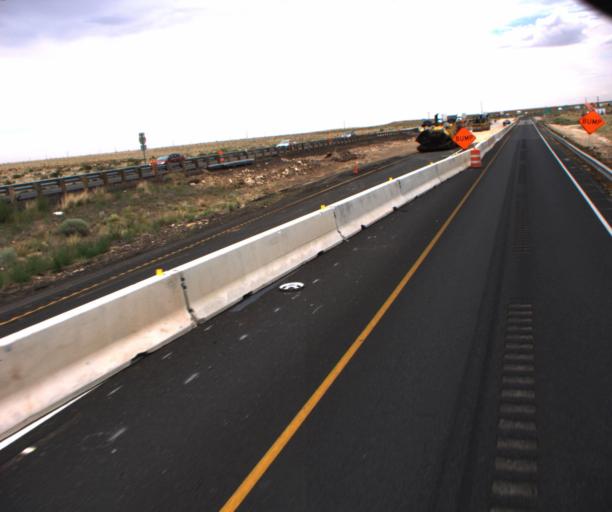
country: US
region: Arizona
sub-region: Coconino County
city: LeChee
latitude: 35.1172
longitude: -111.1019
